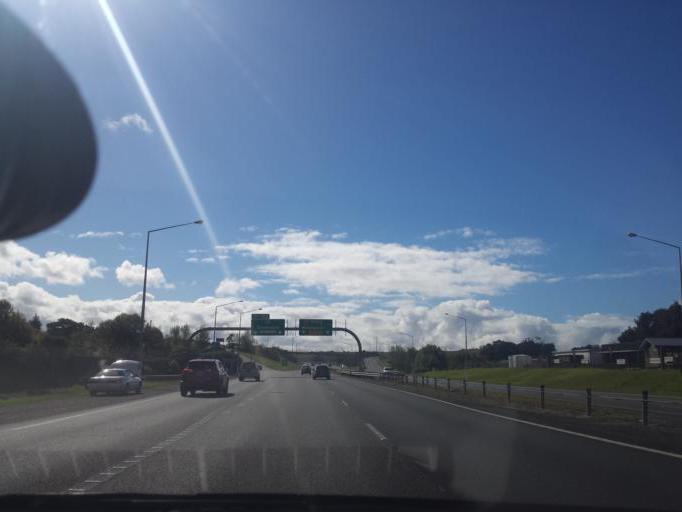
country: NZ
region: Auckland
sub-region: Auckland
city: Rothesay Bay
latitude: -36.6297
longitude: 174.6628
